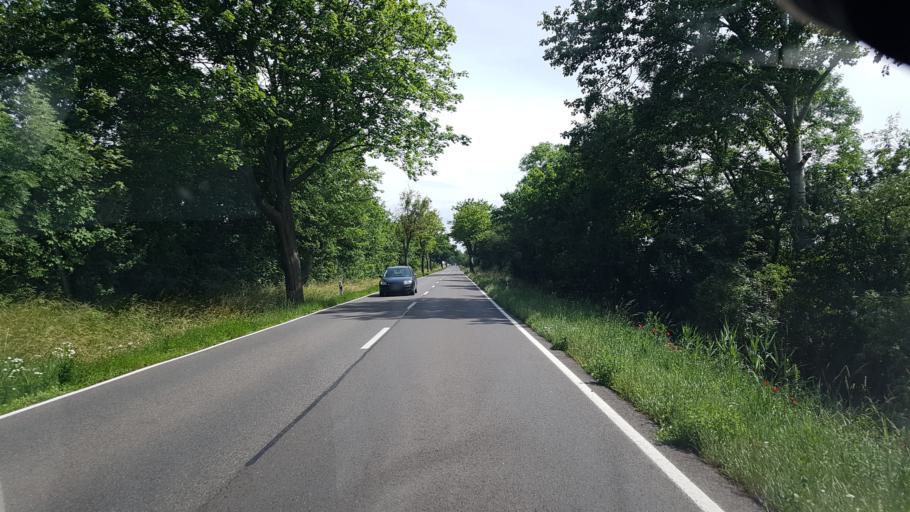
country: DE
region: Brandenburg
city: Prenzlau
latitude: 53.3831
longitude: 13.7783
